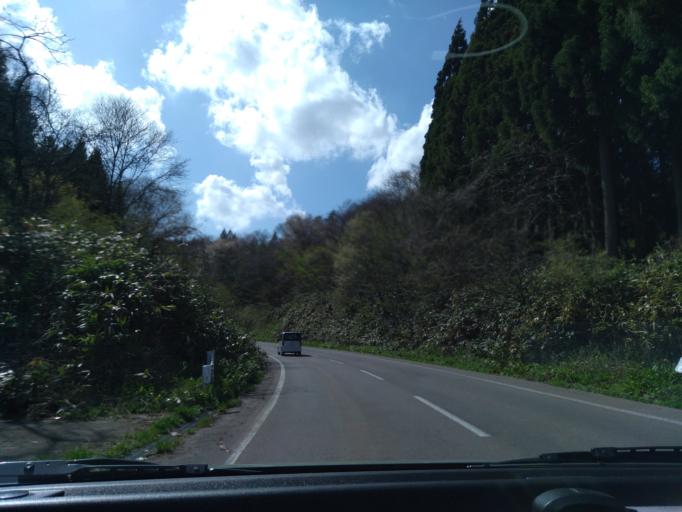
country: JP
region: Akita
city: Akita
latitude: 39.6958
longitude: 140.2682
